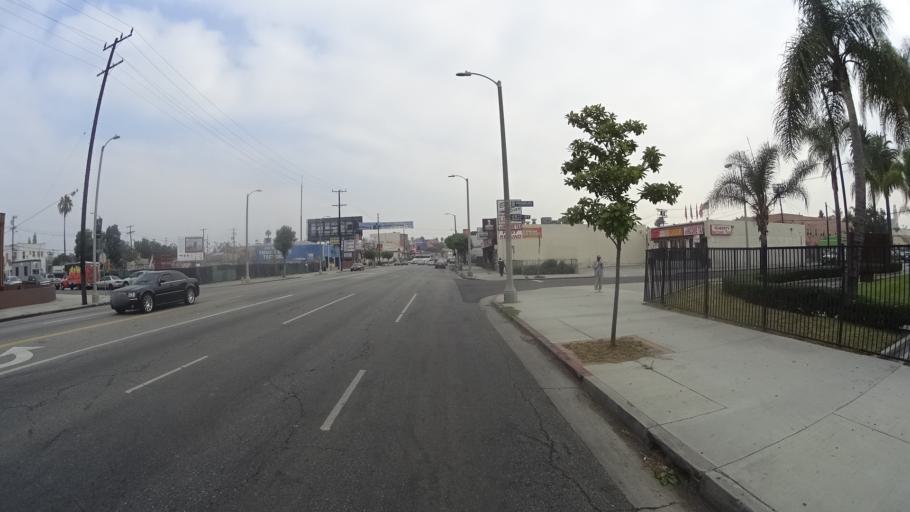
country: US
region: California
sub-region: Los Angeles County
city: View Park-Windsor Hills
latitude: 34.0310
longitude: -118.3351
